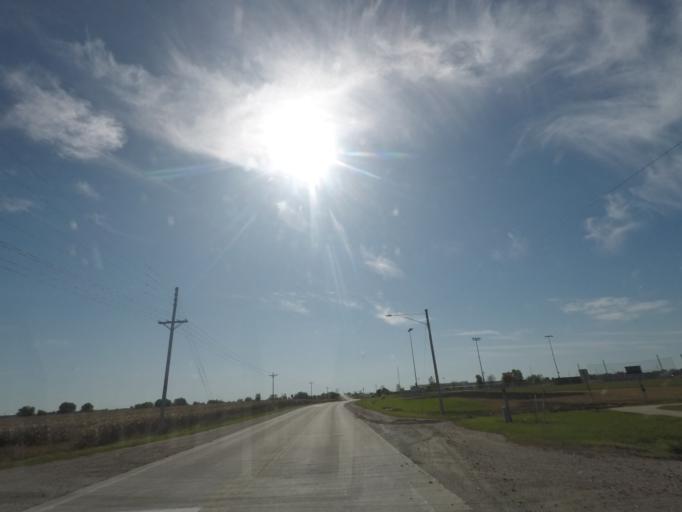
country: US
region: Iowa
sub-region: Story County
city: Nevada
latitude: 42.0163
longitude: -93.4347
